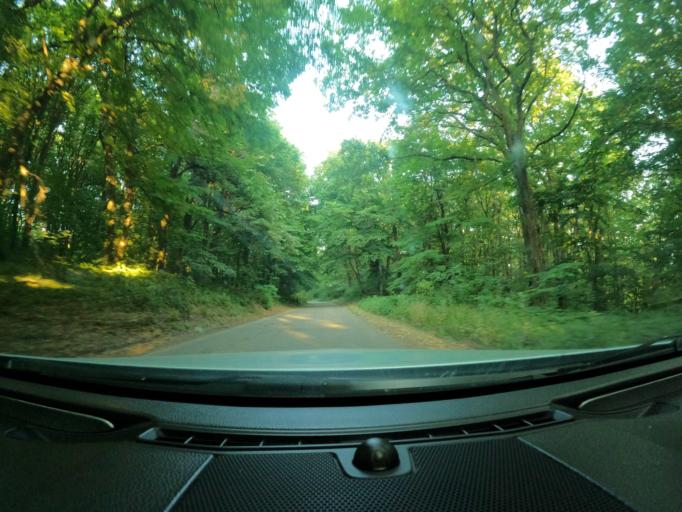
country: RS
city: Vrdnik
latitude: 45.1611
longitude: 19.7603
